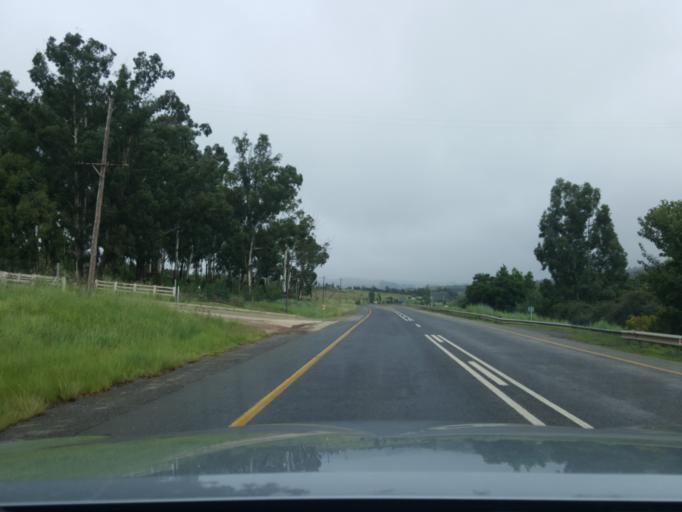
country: ZA
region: Mpumalanga
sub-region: Nkangala District Municipality
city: Belfast
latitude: -25.6139
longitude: 30.2844
